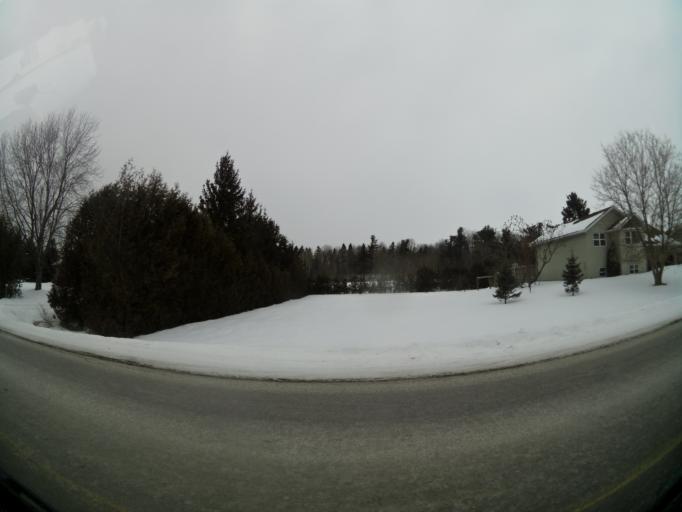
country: CA
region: Ontario
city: Clarence-Rockland
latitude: 45.4150
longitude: -75.4408
